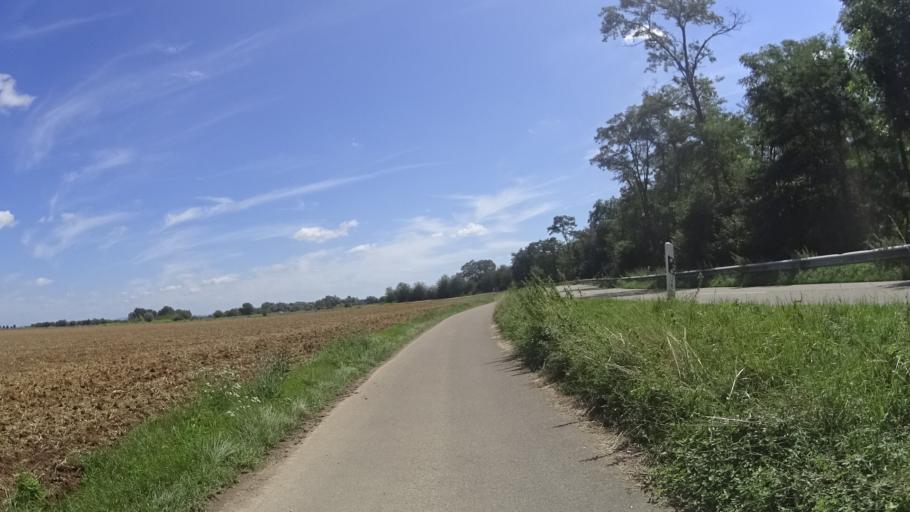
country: DE
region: Rheinland-Pfalz
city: Lingenfeld
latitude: 49.2593
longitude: 8.3636
